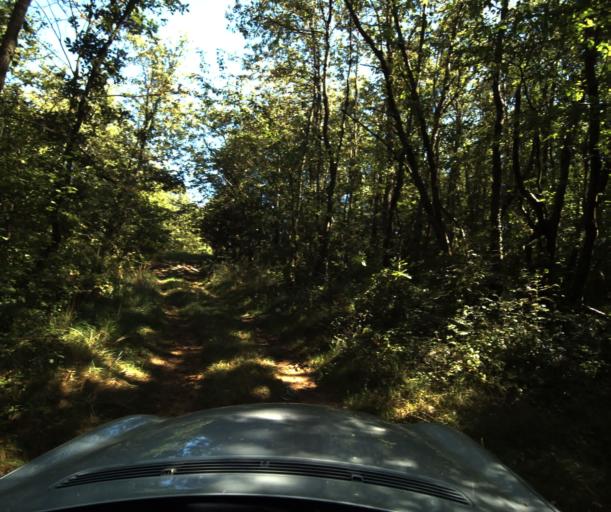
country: FR
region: Midi-Pyrenees
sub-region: Departement de l'Ariege
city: Belesta
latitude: 42.9653
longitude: 1.9235
